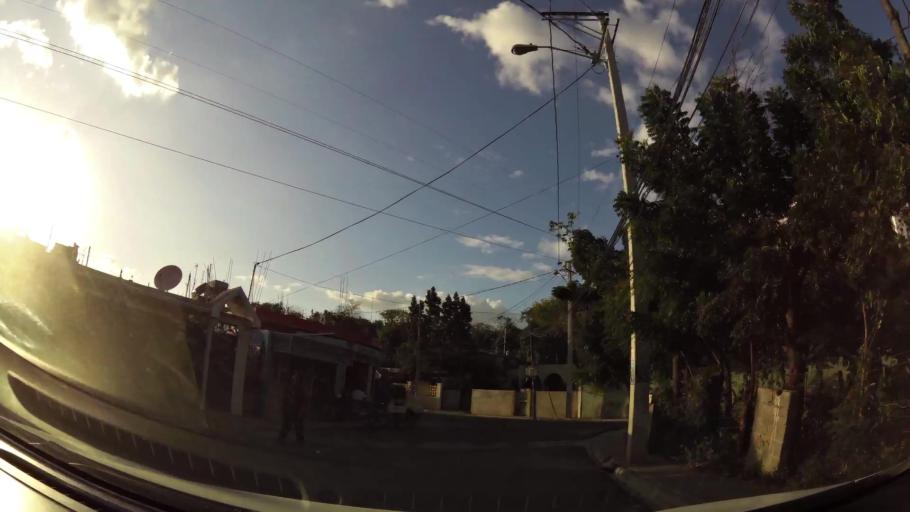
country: DO
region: Santo Domingo
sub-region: Santo Domingo
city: Santo Domingo Este
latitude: 18.4833
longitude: -69.8433
